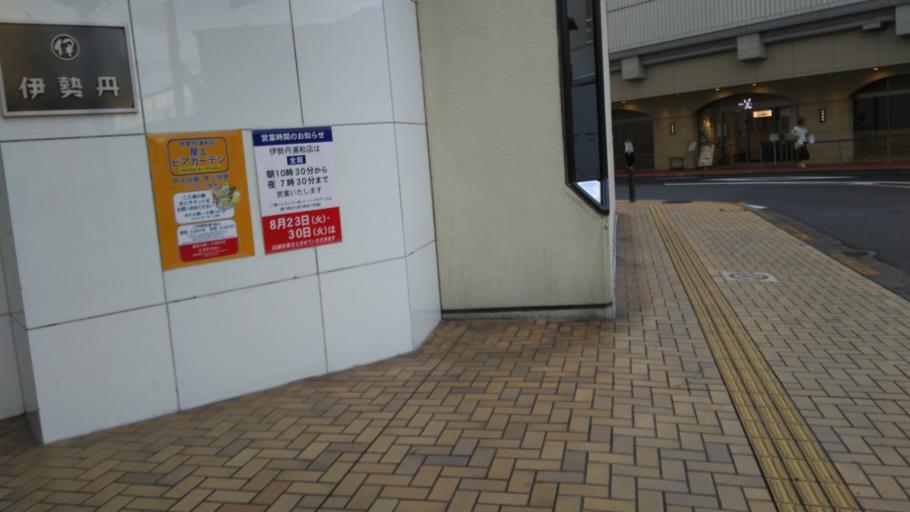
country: JP
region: Saitama
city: Yono
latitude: 35.8589
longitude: 139.6564
